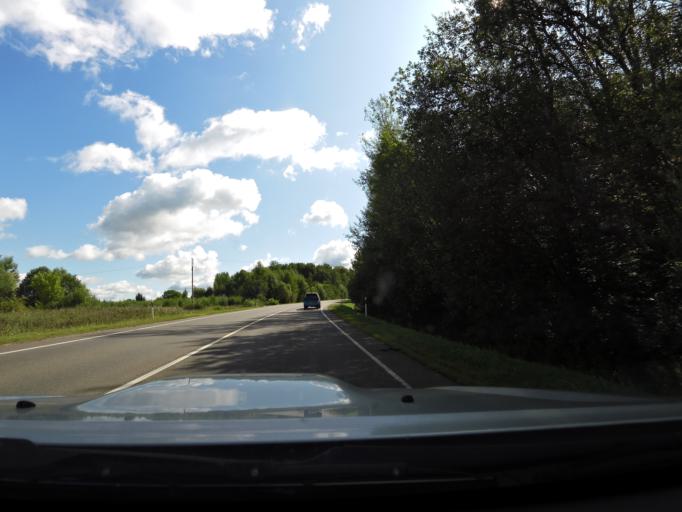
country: LT
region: Utenos apskritis
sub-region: Utena
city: Utena
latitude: 55.4877
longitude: 25.6290
